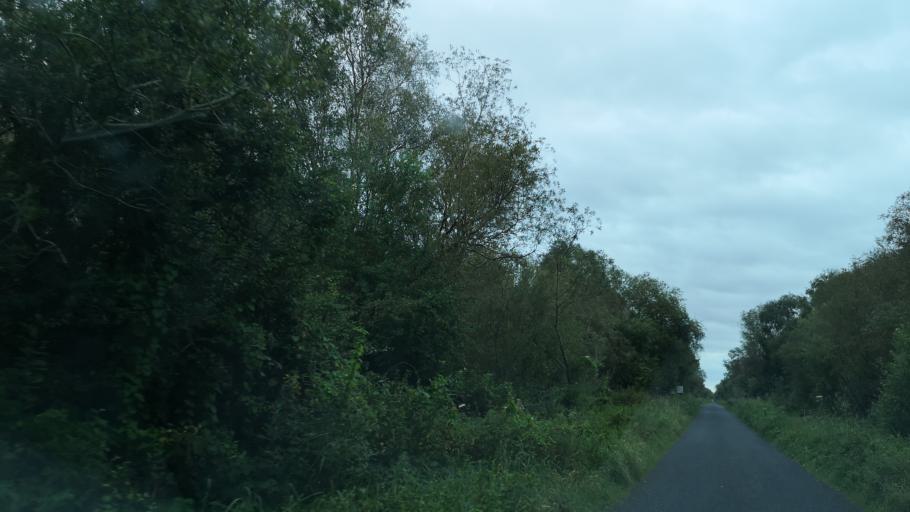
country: IE
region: Leinster
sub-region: Uibh Fhaili
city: Ferbane
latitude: 53.1978
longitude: -7.7254
